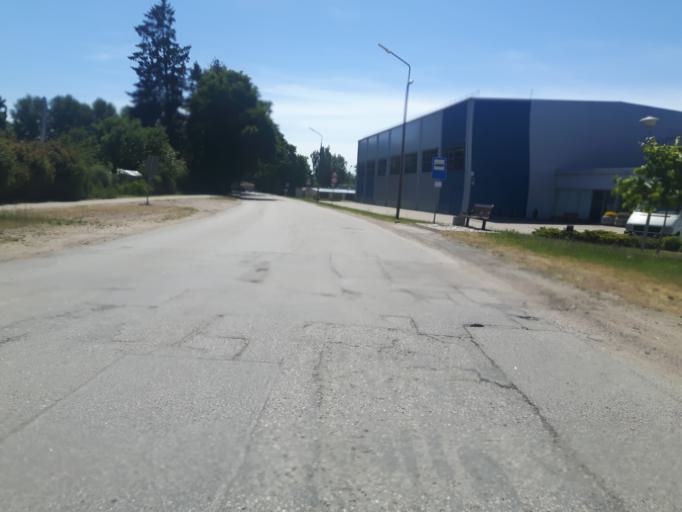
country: LV
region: Grobina
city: Grobina
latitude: 56.5335
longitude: 21.1572
